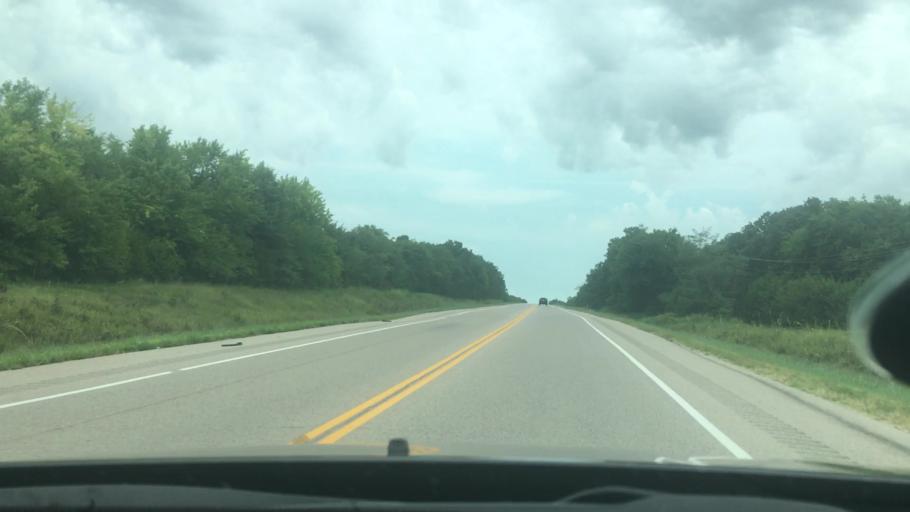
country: US
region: Oklahoma
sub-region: Seminole County
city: Konawa
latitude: 34.9567
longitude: -96.6786
